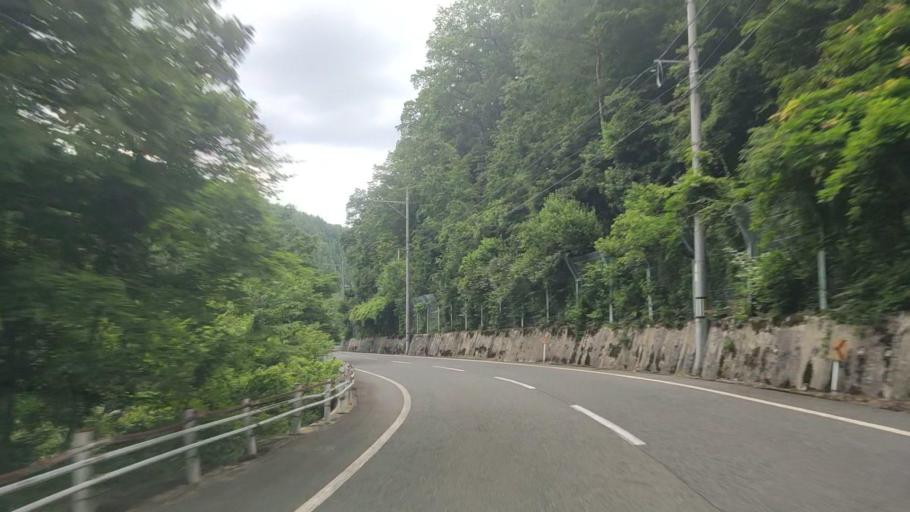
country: JP
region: Tottori
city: Kurayoshi
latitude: 35.2931
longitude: 133.9879
